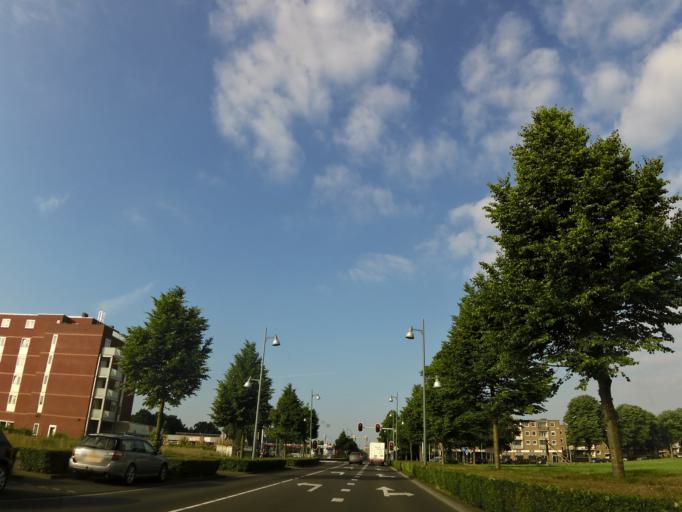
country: NL
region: Limburg
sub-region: Gemeente Sittard-Geleen
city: Limbricht
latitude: 50.9794
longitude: 5.8414
